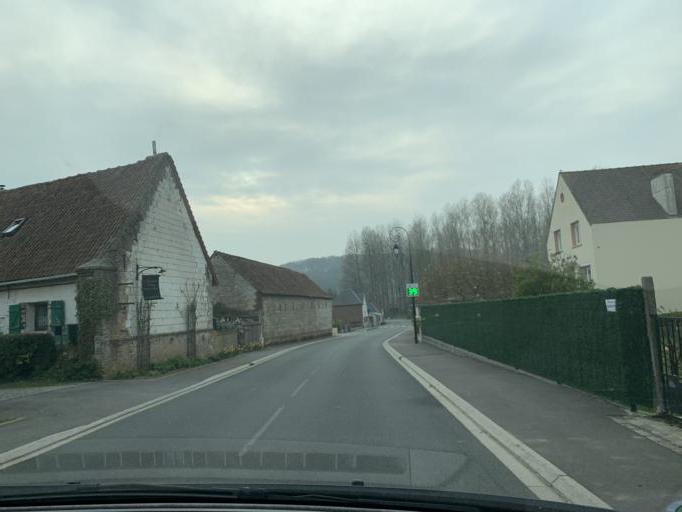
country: FR
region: Nord-Pas-de-Calais
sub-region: Departement du Pas-de-Calais
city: Montreuil
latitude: 50.4994
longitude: 1.7913
